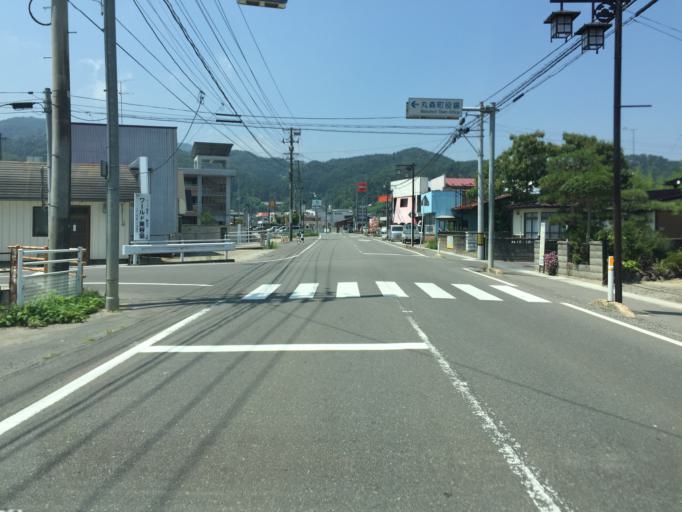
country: JP
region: Miyagi
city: Marumori
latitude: 37.9134
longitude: 140.7677
